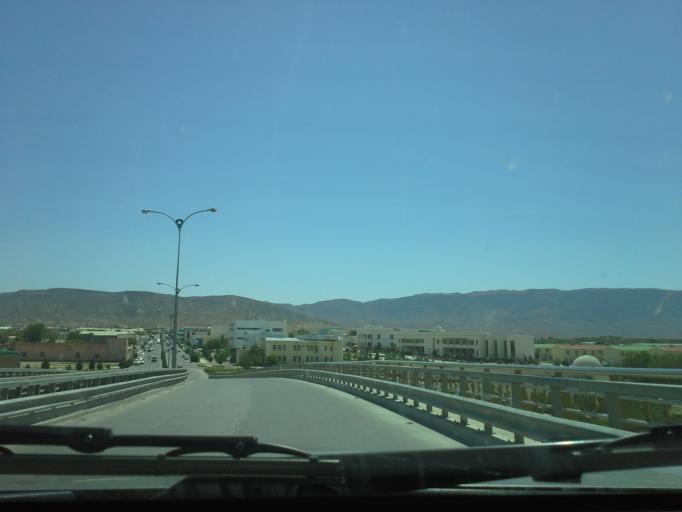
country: TM
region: Balkan
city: Serdar
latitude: 38.9788
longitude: 56.2779
